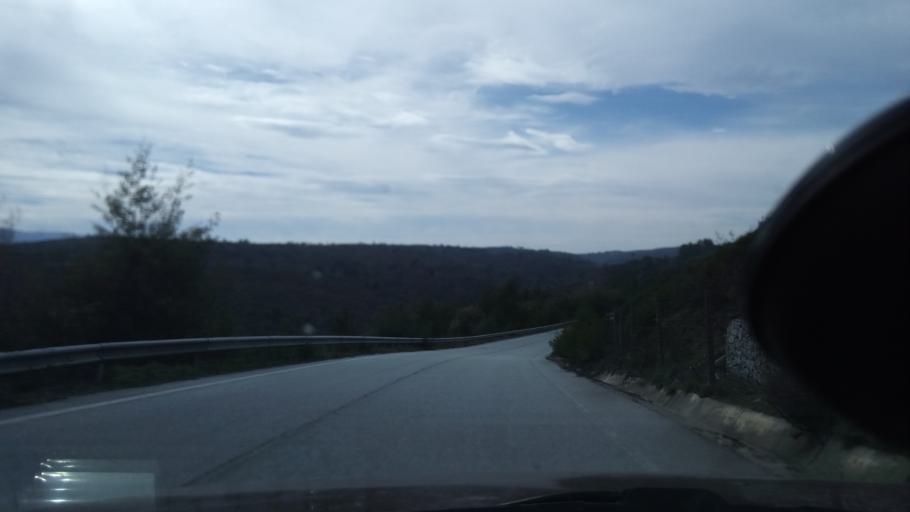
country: PT
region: Guarda
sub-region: Fornos de Algodres
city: Fornos de Algodres
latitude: 40.6093
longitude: -7.5305
